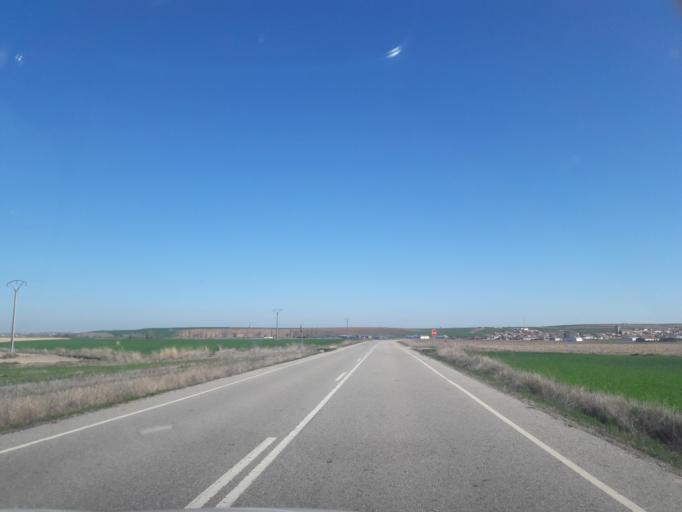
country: ES
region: Castille and Leon
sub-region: Provincia de Salamanca
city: Mancera de Abajo
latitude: 40.8291
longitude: -5.2074
